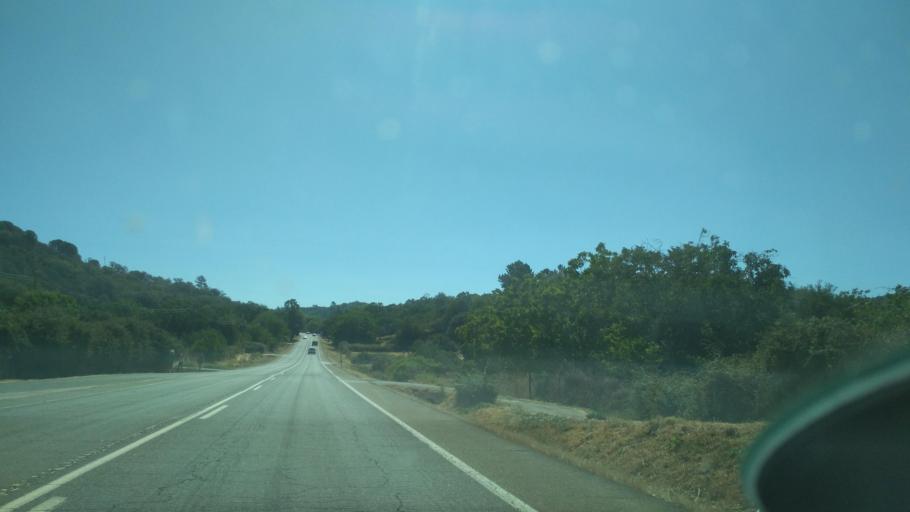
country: ES
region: Andalusia
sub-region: Provincia de Huelva
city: Galaroza
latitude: 37.9213
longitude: -6.6998
